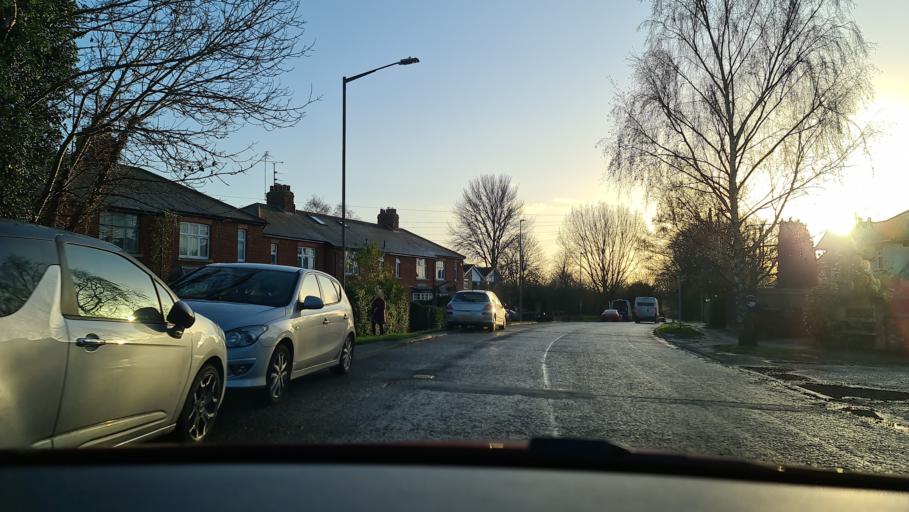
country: GB
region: England
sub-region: Milton Keynes
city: Stony Stratford
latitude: 52.0518
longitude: -0.8503
